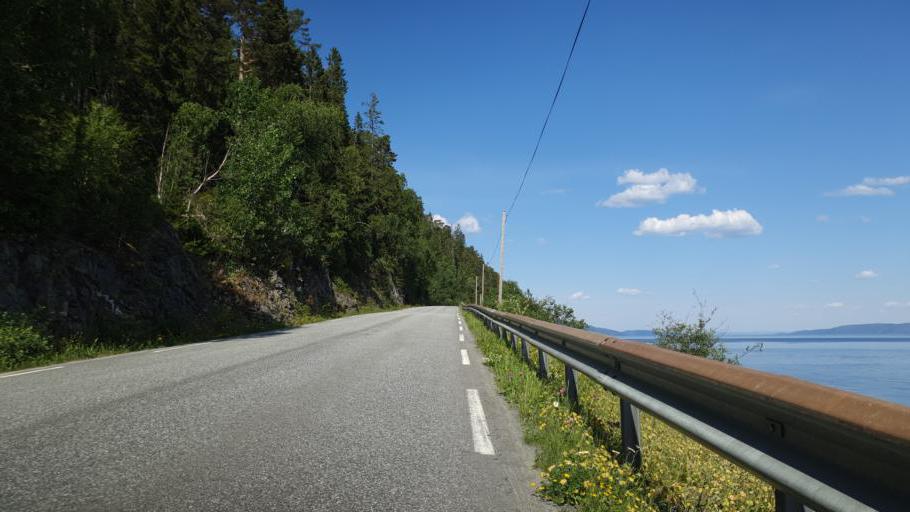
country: NO
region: Nord-Trondelag
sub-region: Leksvik
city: Leksvik
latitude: 63.6424
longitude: 10.5921
